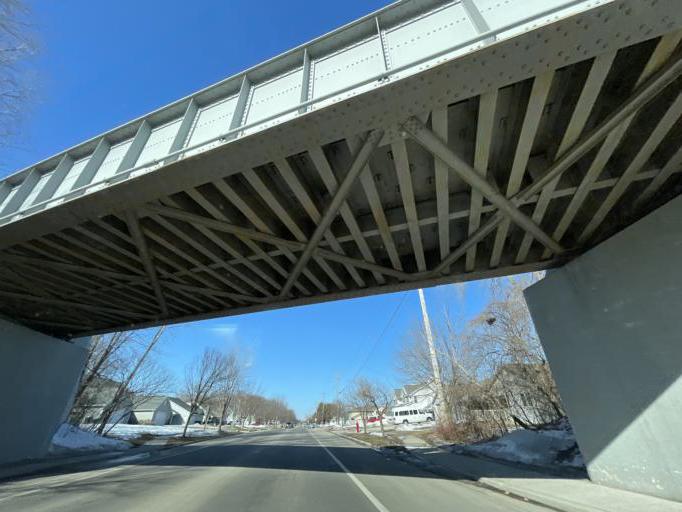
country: US
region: Wisconsin
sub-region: Brown County
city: Howard
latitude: 44.5792
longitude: -88.0845
